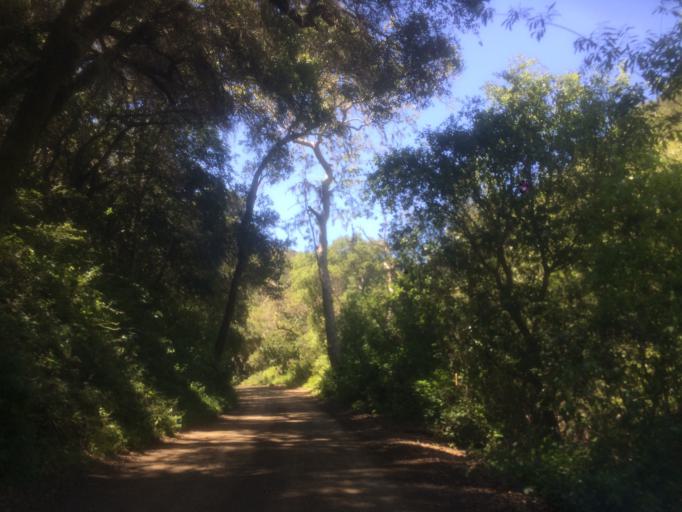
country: US
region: California
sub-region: San Luis Obispo County
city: Templeton
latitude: 35.5252
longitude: -120.7909
